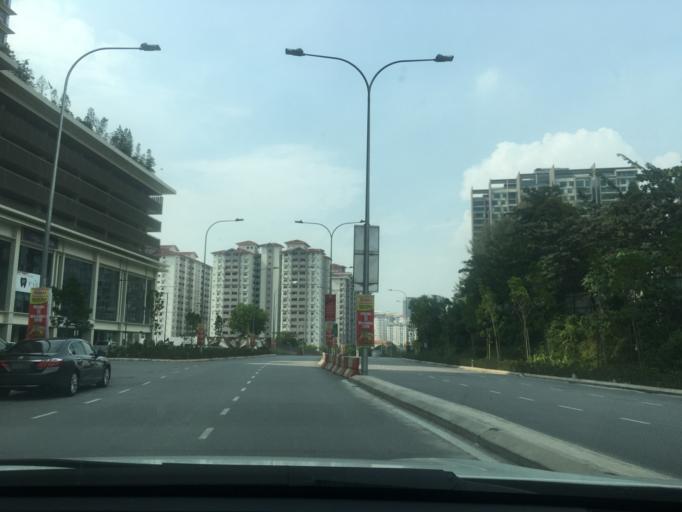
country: MY
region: Selangor
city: Kampong Baharu Balakong
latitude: 3.0536
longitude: 101.6724
